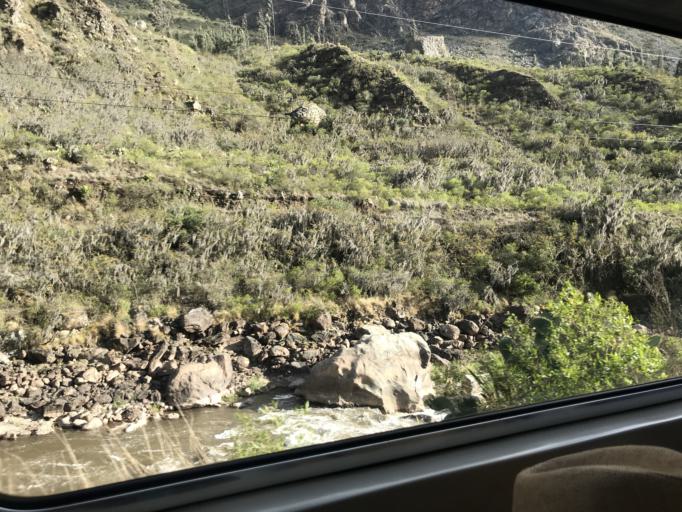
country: PE
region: Cusco
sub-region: Provincia de Urubamba
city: Ollantaytambo
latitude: -13.2262
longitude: -72.3992
